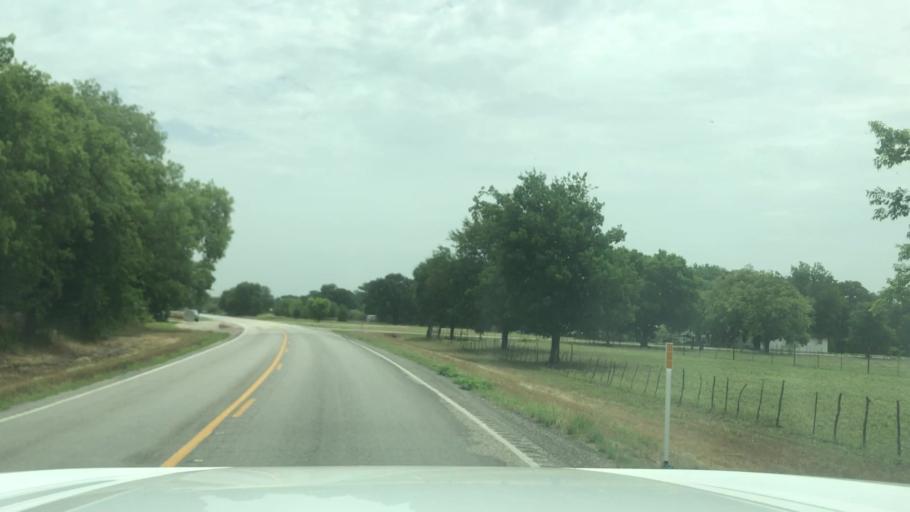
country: US
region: Texas
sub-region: Hamilton County
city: Hico
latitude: 32.0399
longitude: -98.1235
